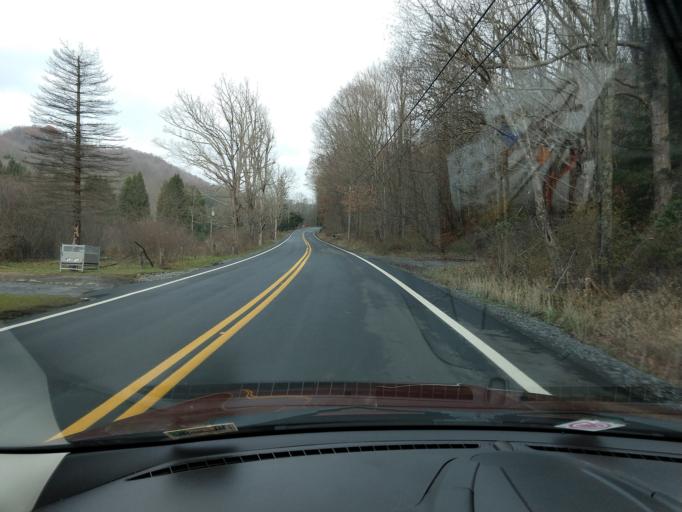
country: US
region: West Virginia
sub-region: Nicholas County
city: Richwood
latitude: 38.1419
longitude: -80.6871
